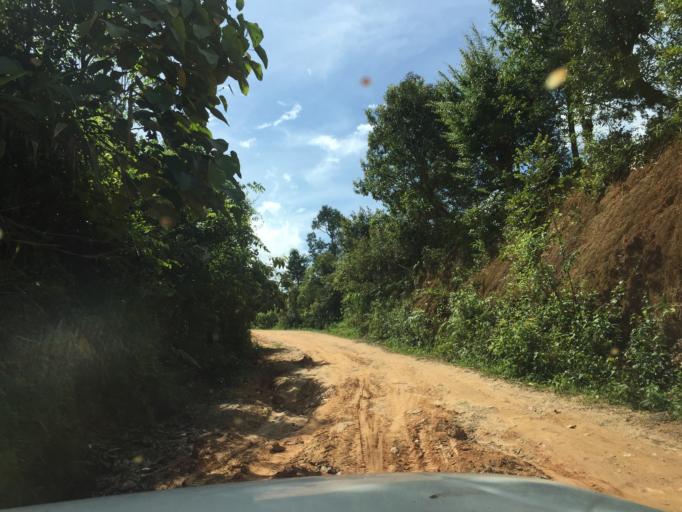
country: LA
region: Xiangkhoang
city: Muang Phonsavan
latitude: 19.3401
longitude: 103.5101
